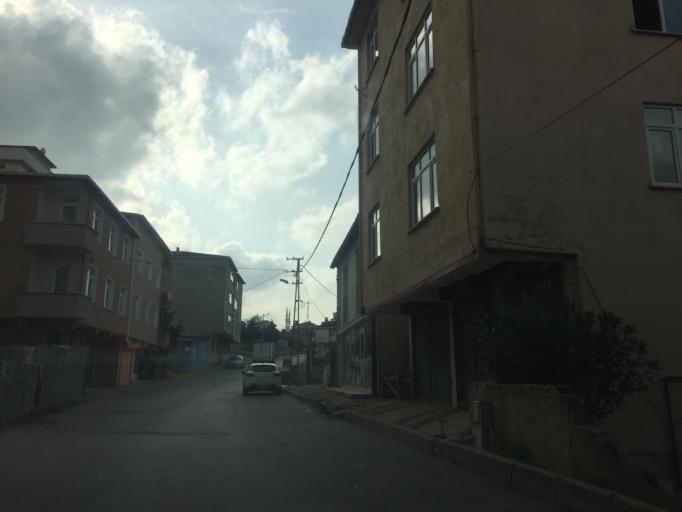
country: TR
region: Istanbul
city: Sultanbeyli
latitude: 40.9413
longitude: 29.2988
